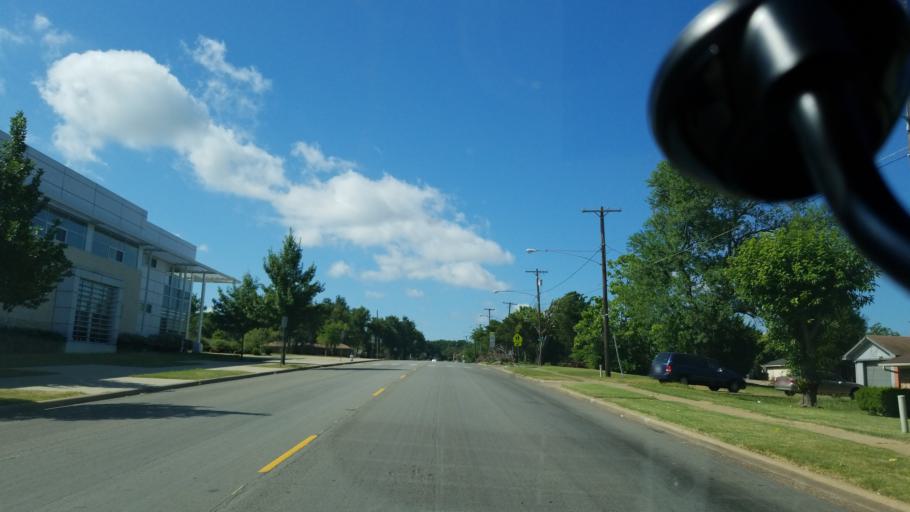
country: US
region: Texas
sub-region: Dallas County
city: Cockrell Hill
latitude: 32.6785
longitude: -96.8147
